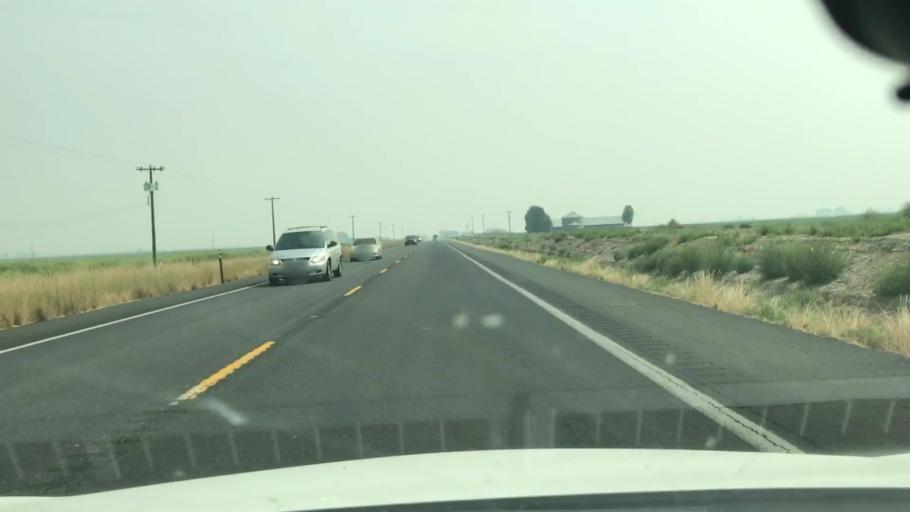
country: US
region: Washington
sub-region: Grant County
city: Quincy
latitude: 47.2341
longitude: -119.8012
